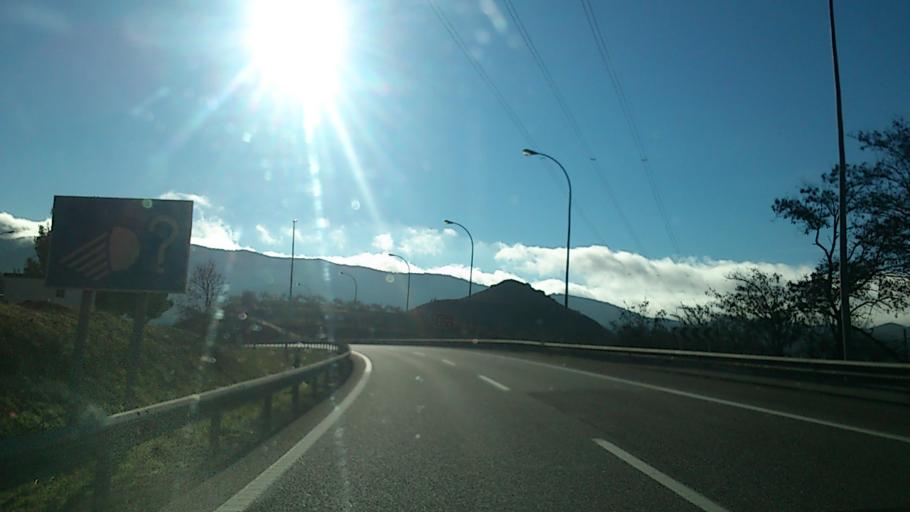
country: ES
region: Aragon
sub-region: Provincia de Zaragoza
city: Morata de Jalon
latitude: 41.4321
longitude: -1.4887
